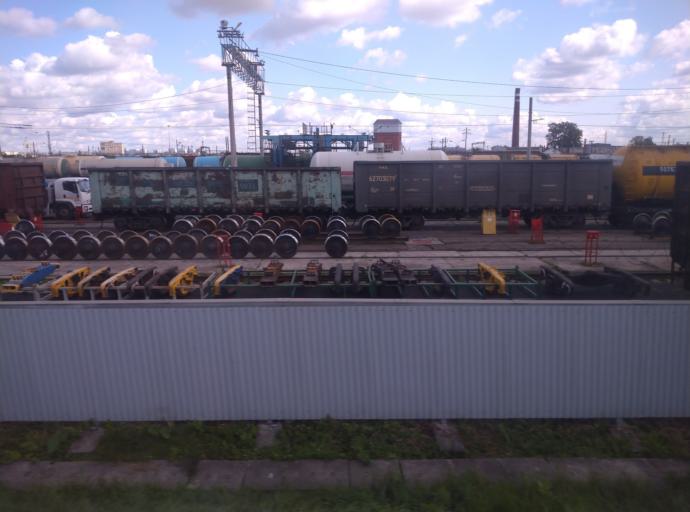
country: RU
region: St.-Petersburg
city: Obukhovo
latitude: 59.8718
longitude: 30.4177
